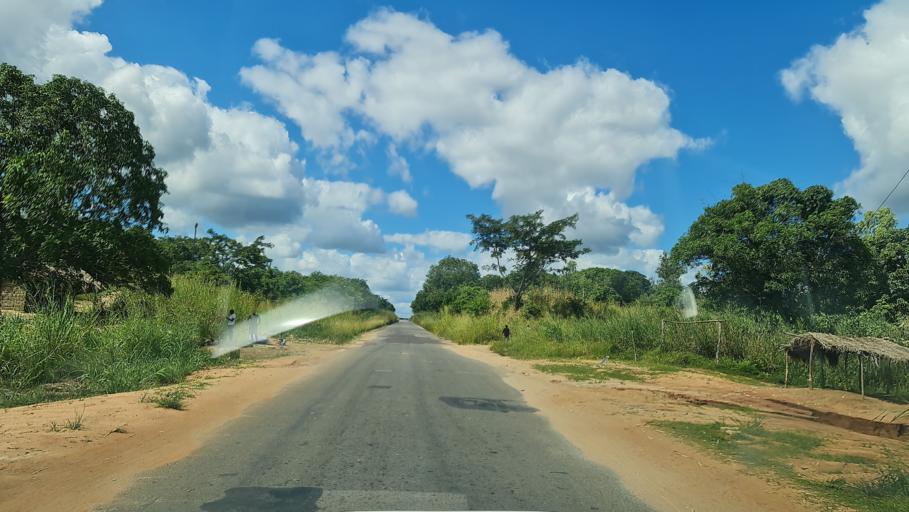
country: MZ
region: Zambezia
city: Quelimane
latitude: -17.5253
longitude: 36.2743
